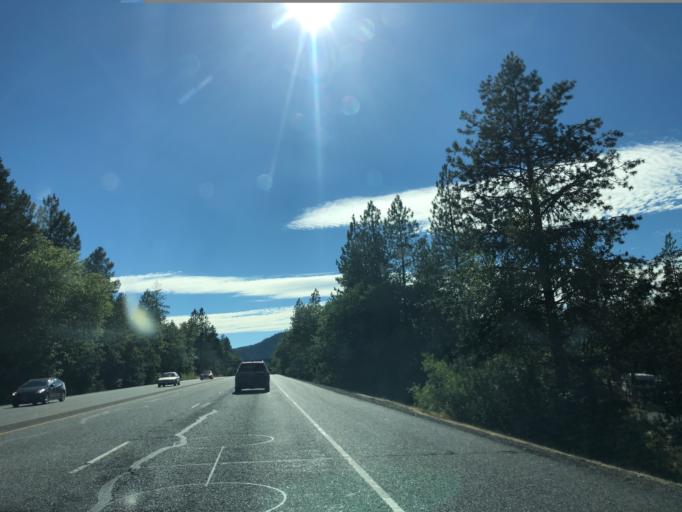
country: US
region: Oregon
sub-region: Josephine County
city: Redwood
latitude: 42.4120
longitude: -123.4168
